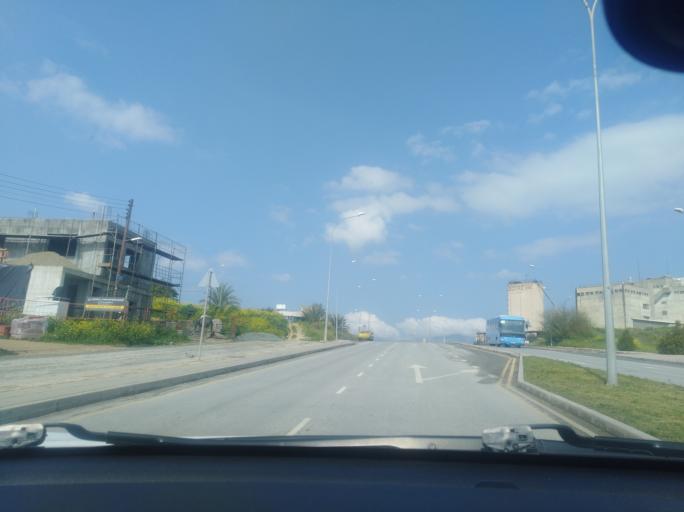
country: CY
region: Lefkosia
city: Nicosia
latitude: 35.1740
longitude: 33.3966
